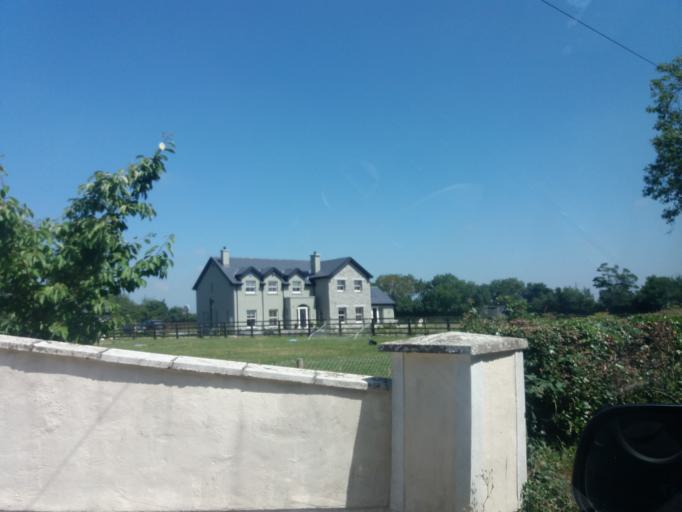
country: IE
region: Leinster
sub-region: Fingal County
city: Swords
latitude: 53.5263
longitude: -6.2373
